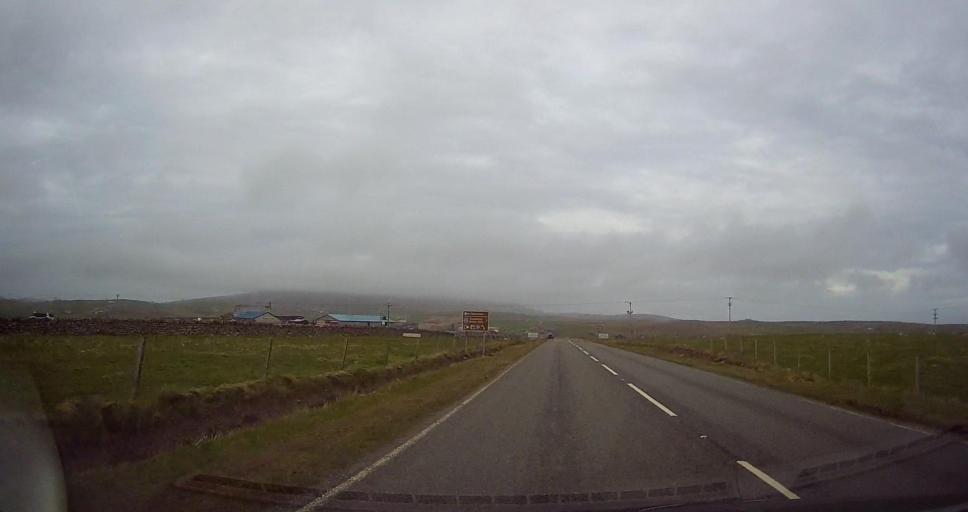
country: GB
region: Scotland
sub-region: Shetland Islands
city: Sandwick
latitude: 59.9167
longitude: -1.3004
